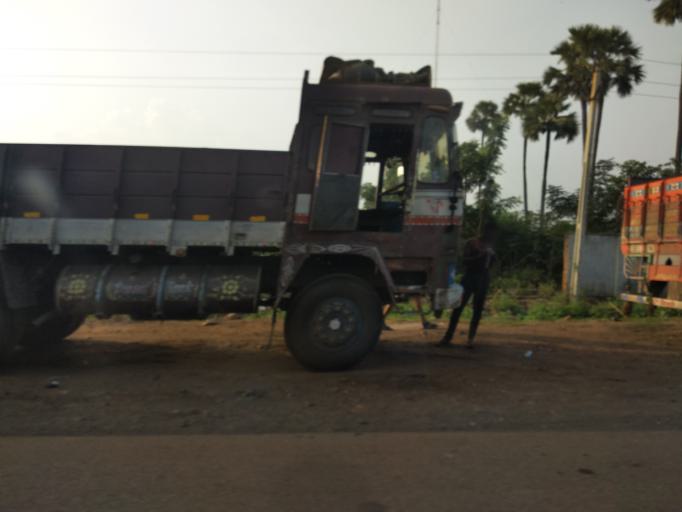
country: IN
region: Andhra Pradesh
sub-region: Vishakhapatnam
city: Visakhapatnam
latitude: 17.6845
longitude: 83.1614
